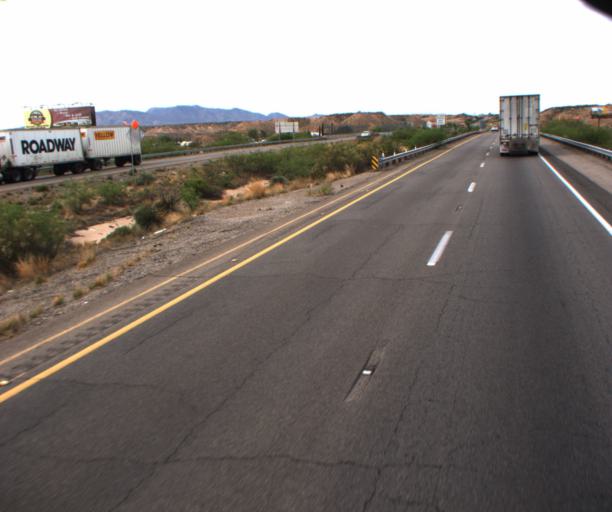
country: US
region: Arizona
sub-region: Cochise County
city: Benson
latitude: 31.9770
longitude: -110.3153
